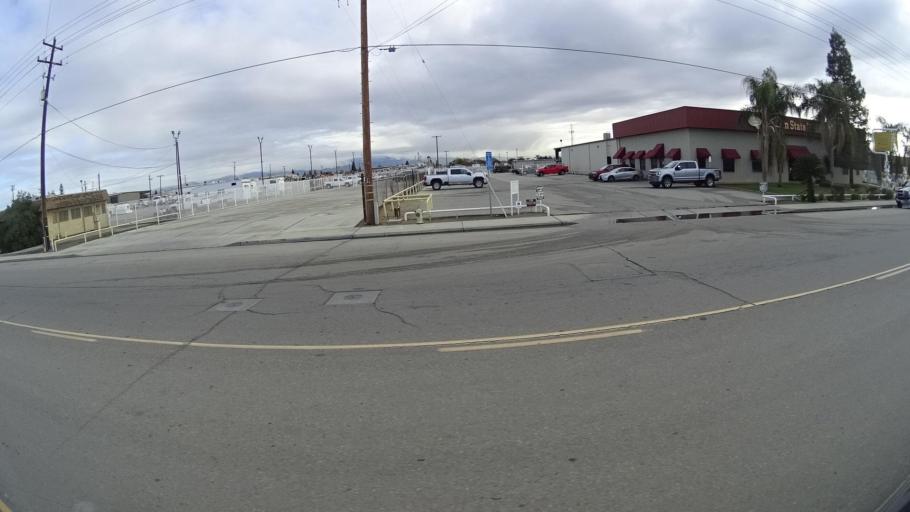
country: US
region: California
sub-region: Kern County
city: Greenacres
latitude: 35.3925
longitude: -119.0744
